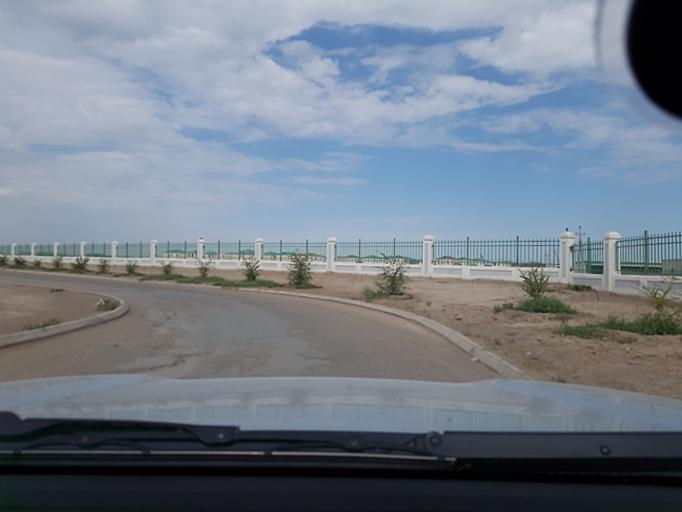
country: TM
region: Dasoguz
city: Dasoguz
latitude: 41.8812
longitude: 59.9502
